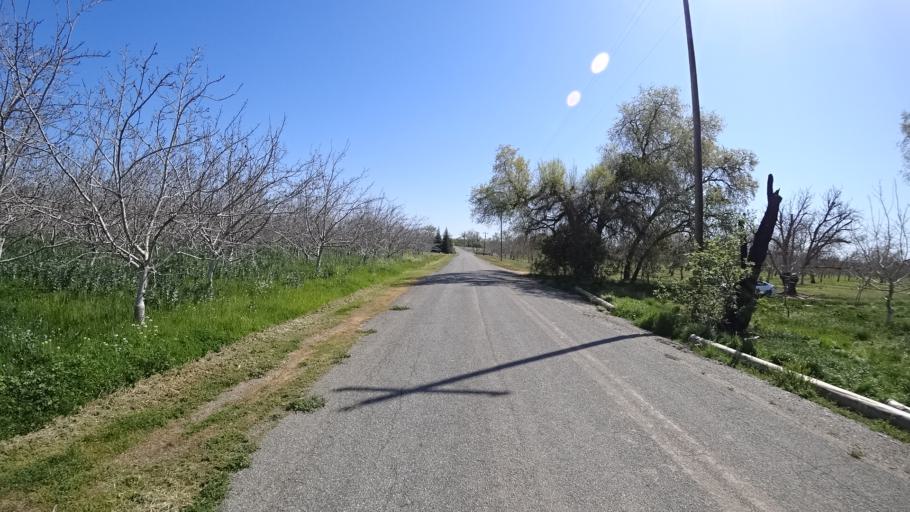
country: US
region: California
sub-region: Glenn County
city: Willows
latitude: 39.4429
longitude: -122.0182
